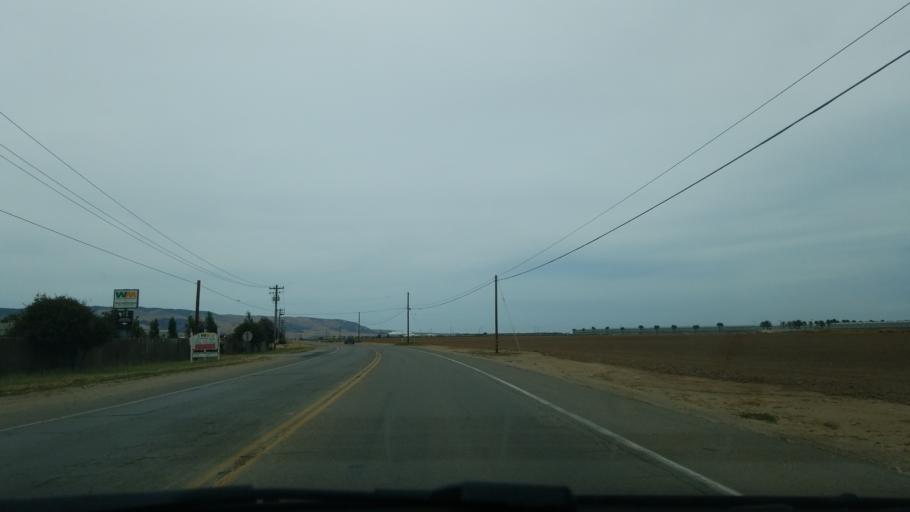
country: US
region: California
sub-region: Santa Barbara County
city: Santa Maria
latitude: 34.9213
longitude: -120.4777
